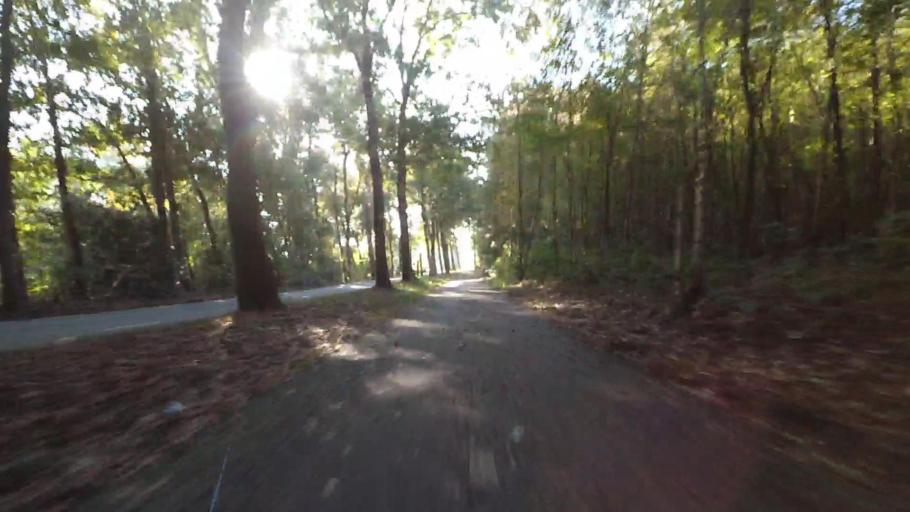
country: NL
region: Gelderland
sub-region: Gemeente Putten
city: Putten
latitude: 52.2767
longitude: 5.6046
